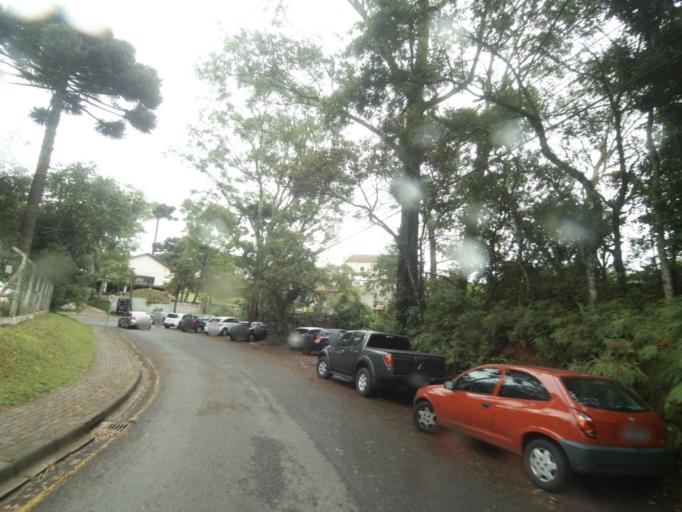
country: BR
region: Parana
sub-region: Curitiba
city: Curitiba
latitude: -25.4430
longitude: -49.3391
